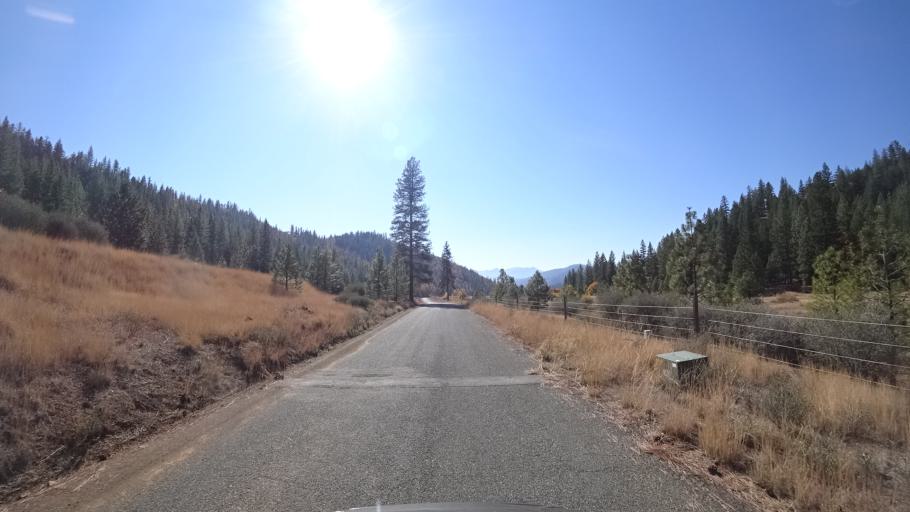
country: US
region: California
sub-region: Siskiyou County
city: Yreka
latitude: 41.6517
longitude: -122.8827
